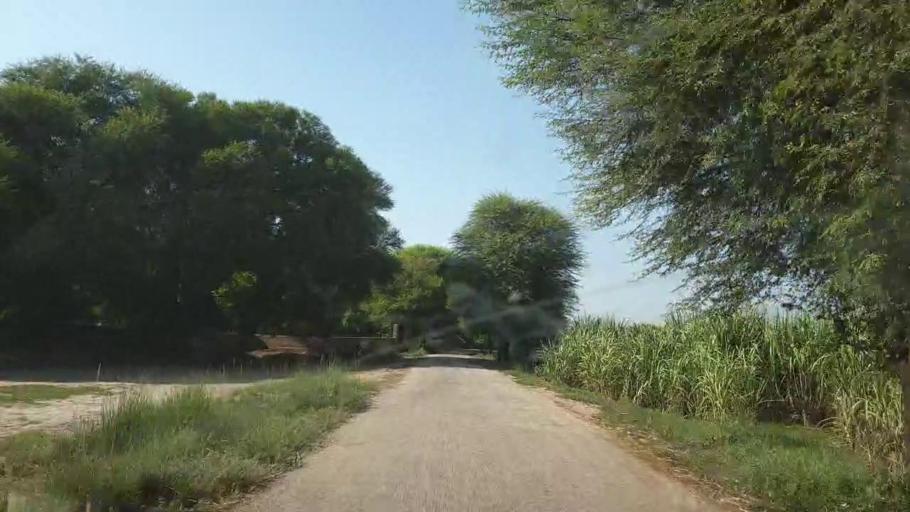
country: PK
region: Sindh
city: Tando Jam
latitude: 25.3453
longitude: 68.5828
